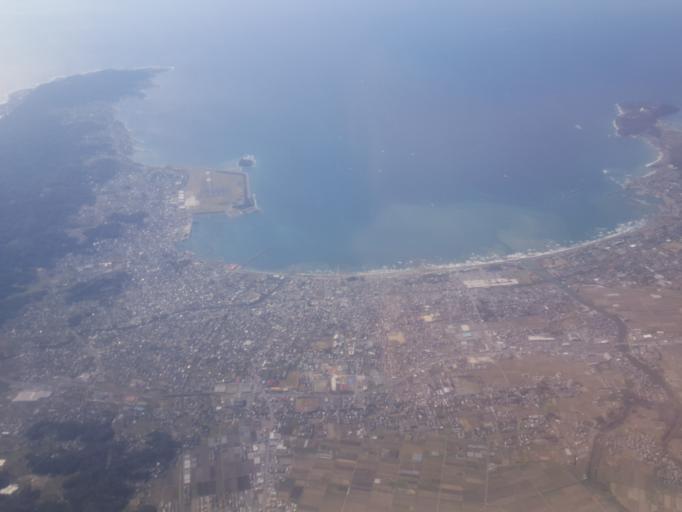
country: JP
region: Chiba
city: Tateyama
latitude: 34.9913
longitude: 139.9082
